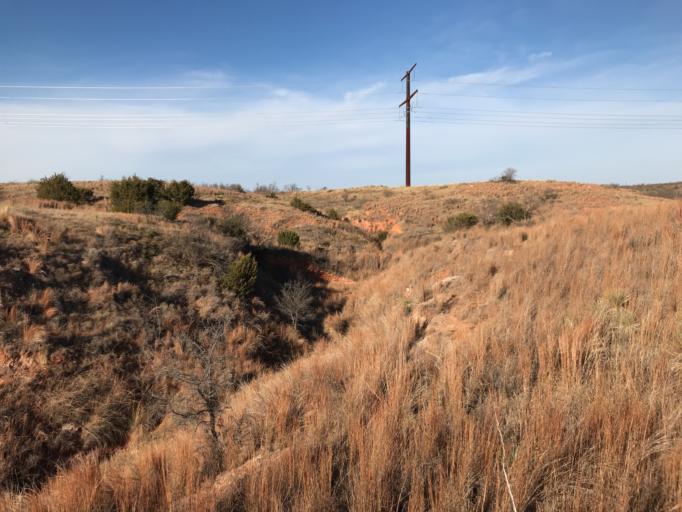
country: US
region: Texas
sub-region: Childress County
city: Childress
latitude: 34.3334
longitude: -100.4816
